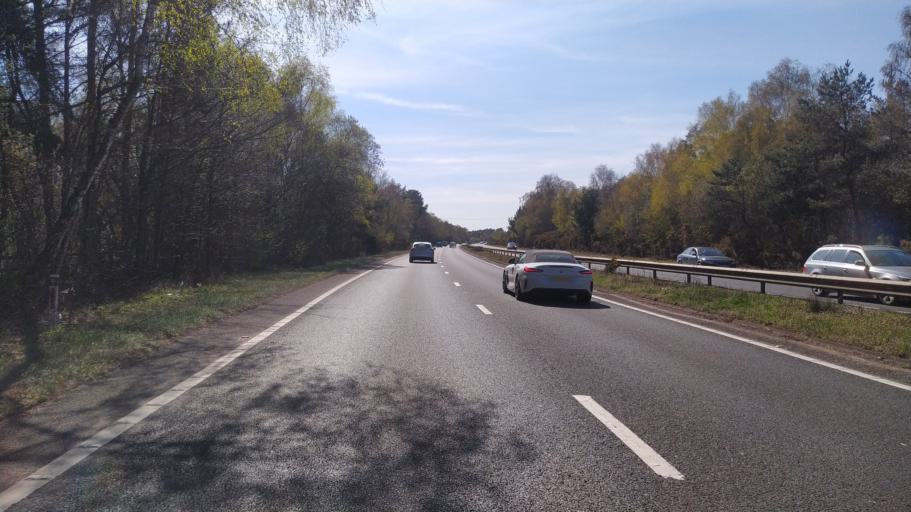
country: GB
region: England
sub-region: Hampshire
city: Liphook
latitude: 51.0788
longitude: -0.8377
